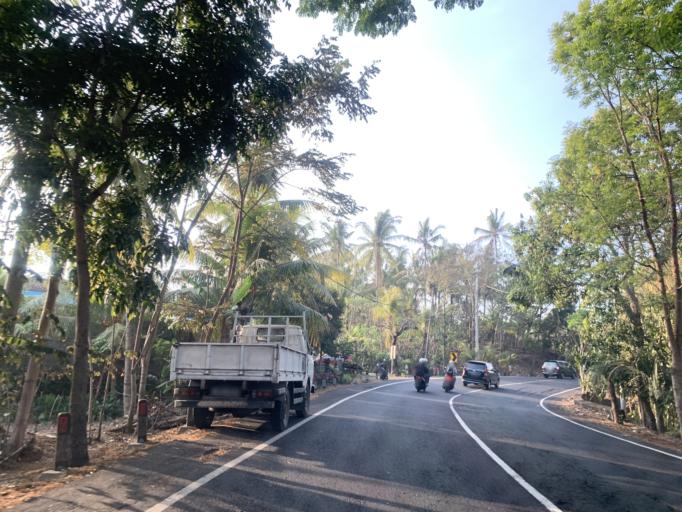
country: ID
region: Bali
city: Banjar Delodrurung
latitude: -8.5006
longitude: 115.0209
